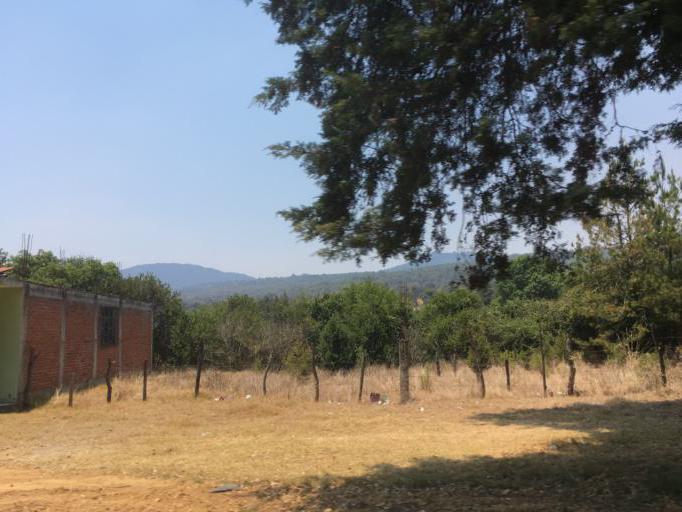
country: MX
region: Michoacan
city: Quiroga
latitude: 19.6361
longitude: -101.4742
